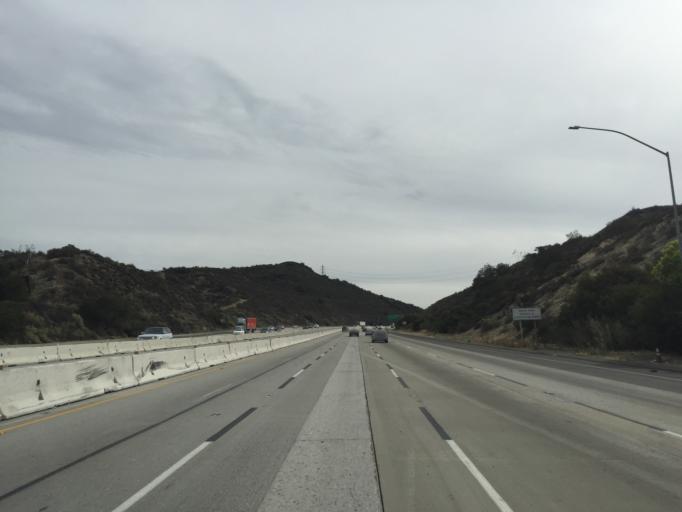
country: US
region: California
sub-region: Los Angeles County
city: Burbank
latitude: 34.2558
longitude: -118.3263
